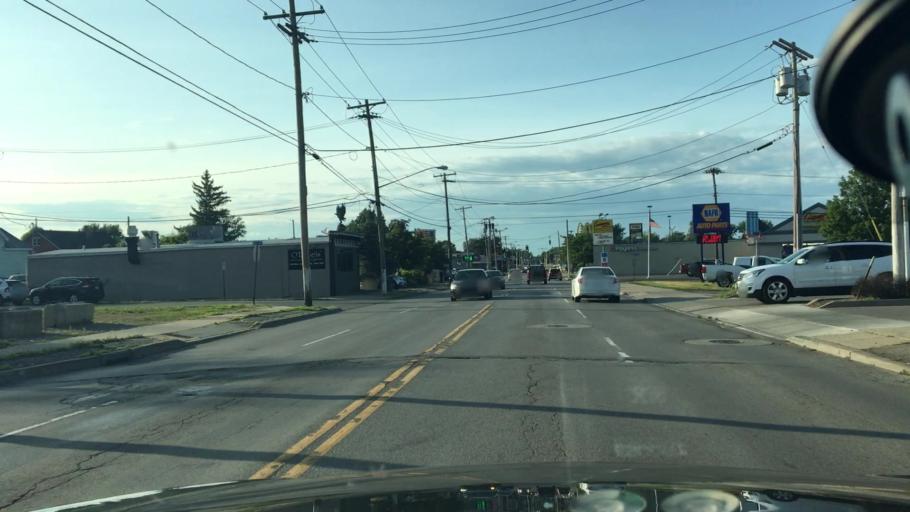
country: US
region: New York
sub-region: Erie County
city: Lackawanna
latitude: 42.8288
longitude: -78.8046
